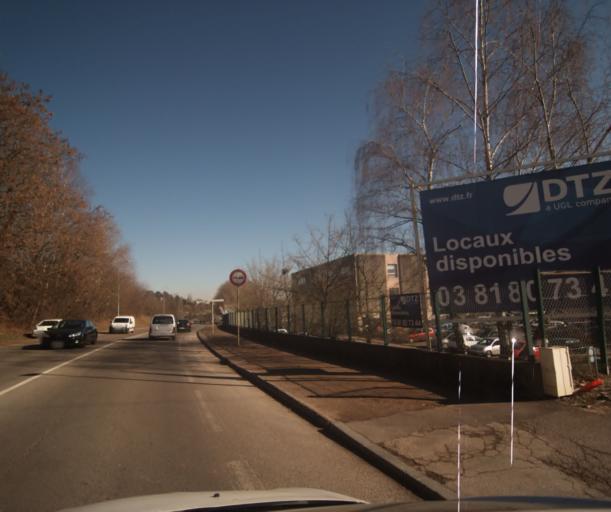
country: FR
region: Franche-Comte
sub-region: Departement du Doubs
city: Avanne-Aveney
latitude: 47.2299
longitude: 5.9666
